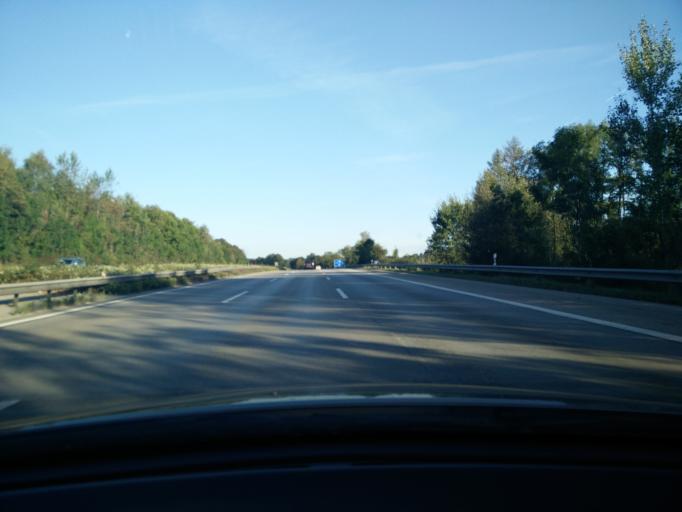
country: DE
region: Bavaria
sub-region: Upper Bavaria
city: Vagen
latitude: 47.8530
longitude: 11.8622
